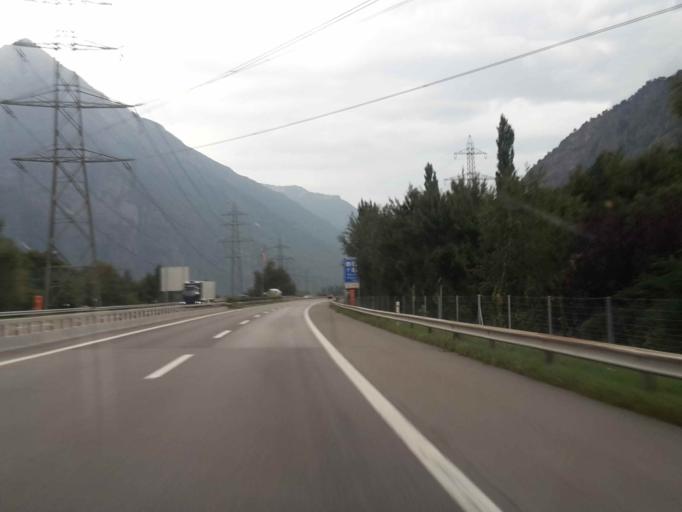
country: CH
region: Valais
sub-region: Martigny District
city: Martigny-Ville
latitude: 46.1194
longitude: 7.0689
